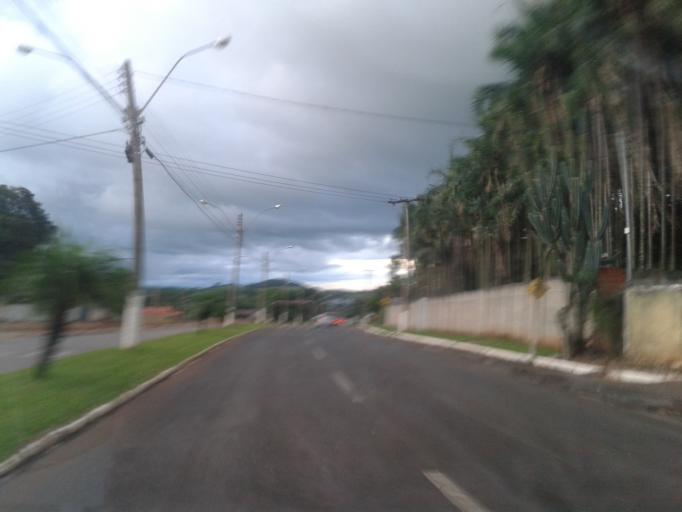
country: BR
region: Goias
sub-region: Morrinhos
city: Morrinhos
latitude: -17.7299
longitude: -49.1499
